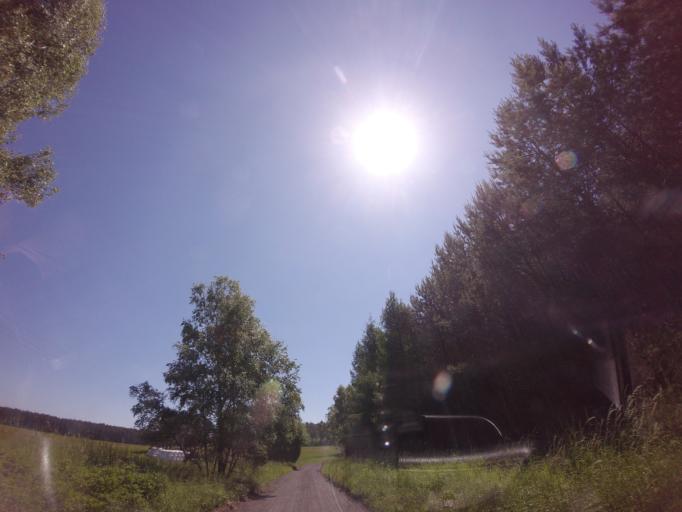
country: PL
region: West Pomeranian Voivodeship
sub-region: Powiat walecki
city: Miroslawiec
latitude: 53.2434
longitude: 16.0355
